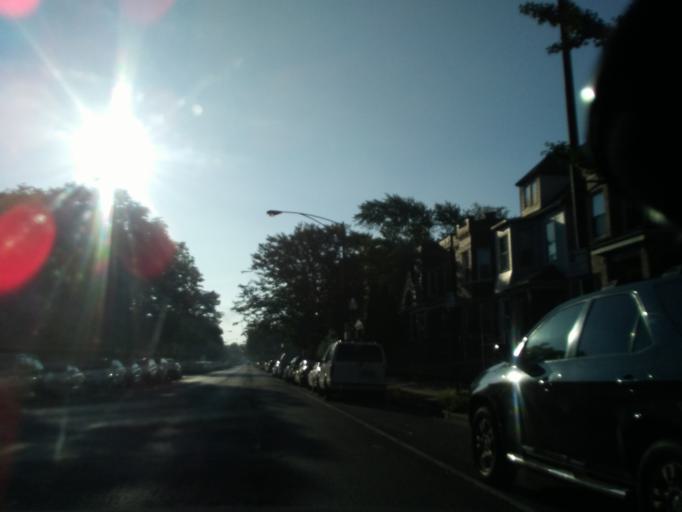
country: US
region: Illinois
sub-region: Cook County
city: Lincolnwood
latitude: 41.9282
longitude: -87.7204
